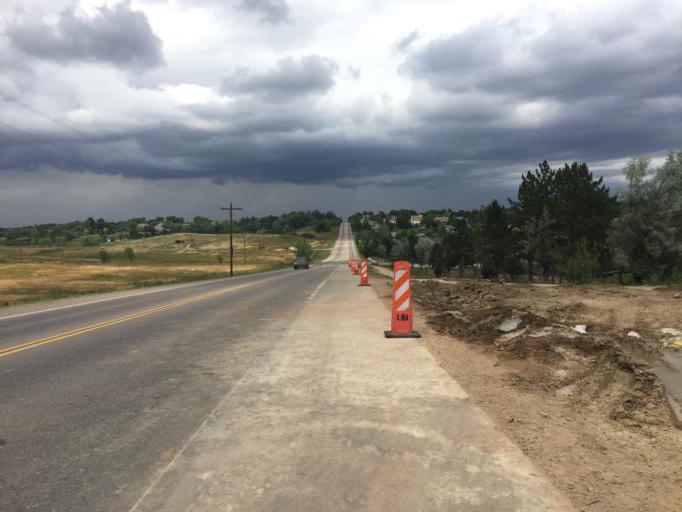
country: US
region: Colorado
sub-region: Larimer County
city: Fort Collins
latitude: 40.5073
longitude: -105.0962
